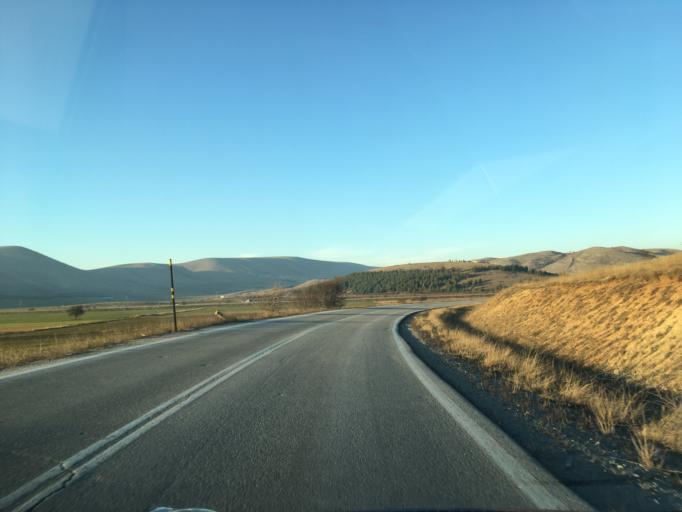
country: GR
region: West Macedonia
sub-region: Nomos Kozanis
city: Kozani
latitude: 40.3118
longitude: 21.7312
